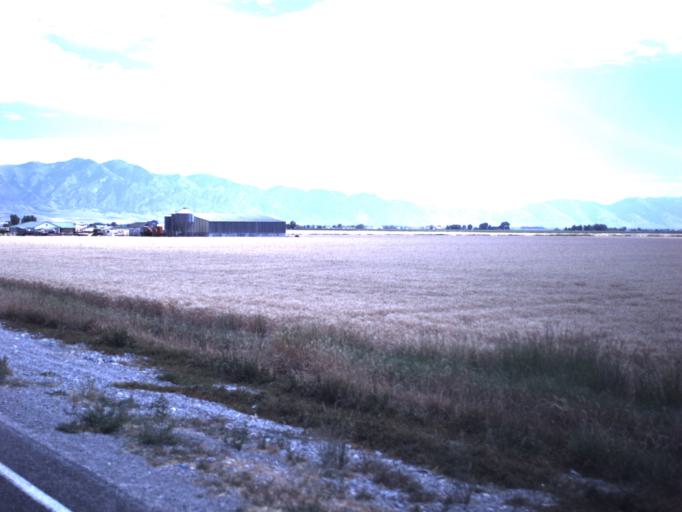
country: US
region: Utah
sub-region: Box Elder County
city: Tremonton
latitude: 41.7098
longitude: -112.2539
